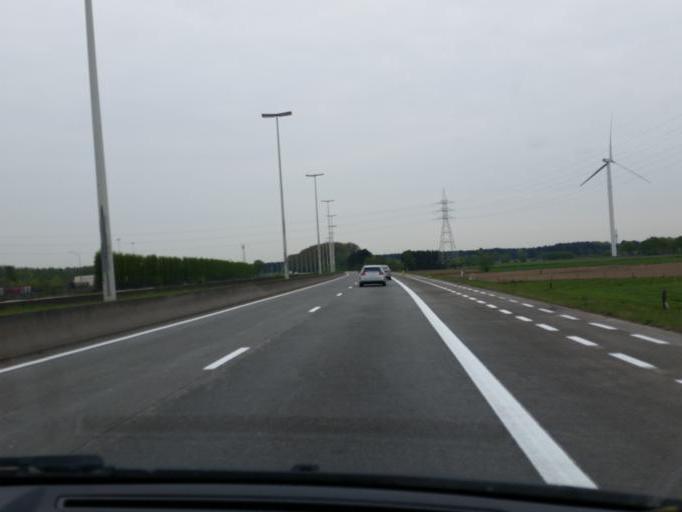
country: BE
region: Flanders
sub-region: Provincie Oost-Vlaanderen
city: Zelzate
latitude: 51.1690
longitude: 3.8275
